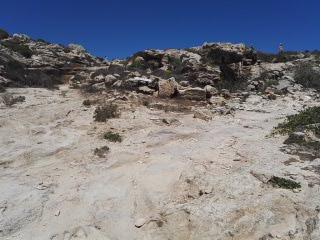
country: IT
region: Sicily
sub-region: Trapani
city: Favignana
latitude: 37.9172
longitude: 12.3696
